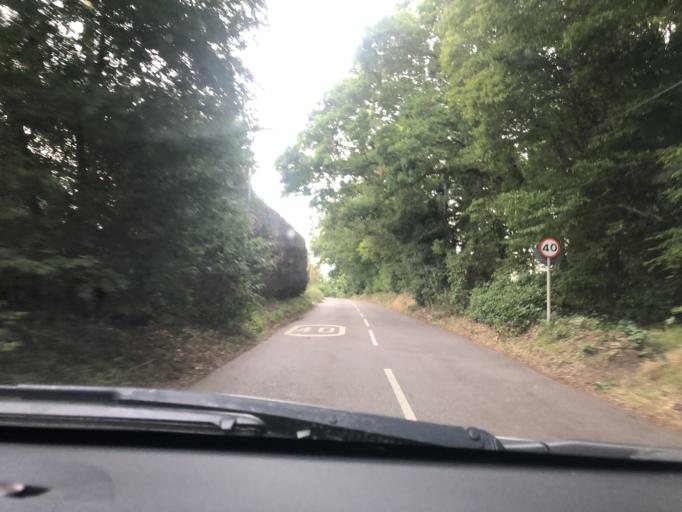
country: GB
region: England
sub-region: Kent
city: Sturry
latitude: 51.3094
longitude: 1.1357
